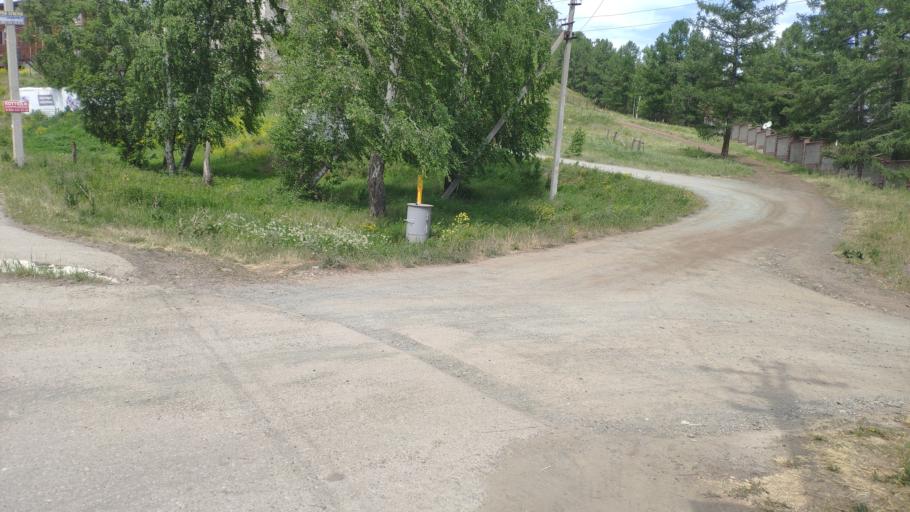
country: RU
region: Bashkortostan
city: Abzakovo
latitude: 53.8119
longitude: 58.6348
